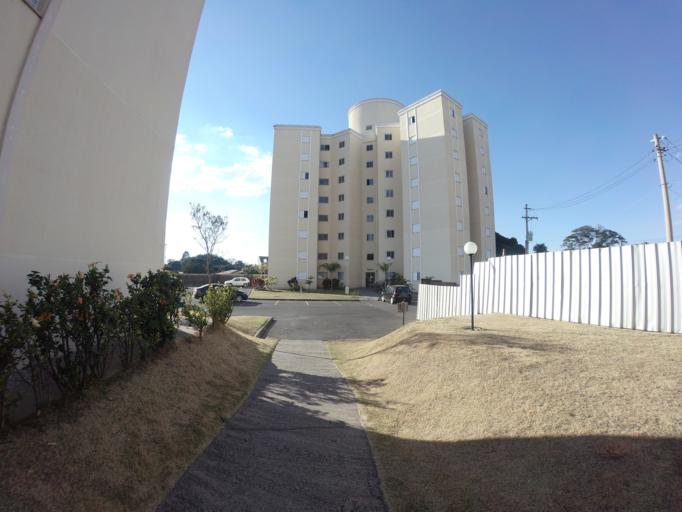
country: BR
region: Sao Paulo
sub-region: Piracicaba
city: Piracicaba
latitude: -22.7395
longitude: -47.5964
